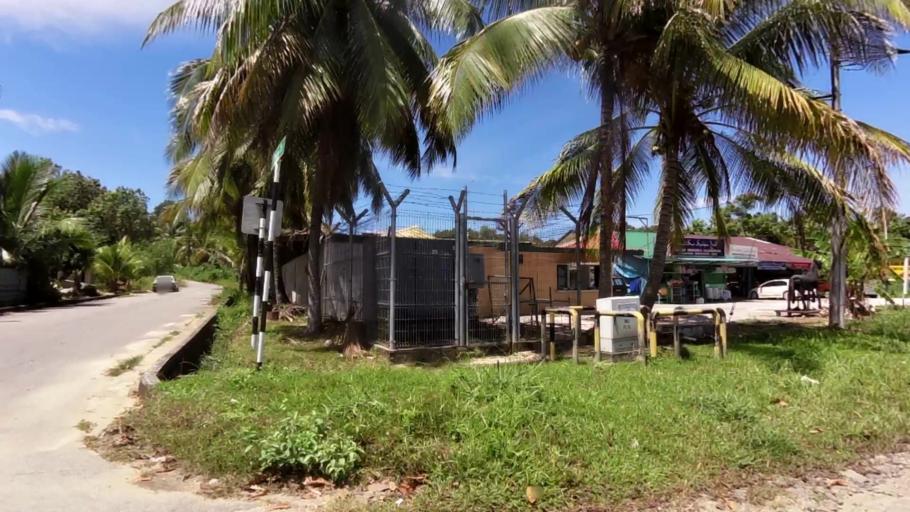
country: BN
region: Brunei and Muara
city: Bandar Seri Begawan
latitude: 4.9345
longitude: 114.9557
